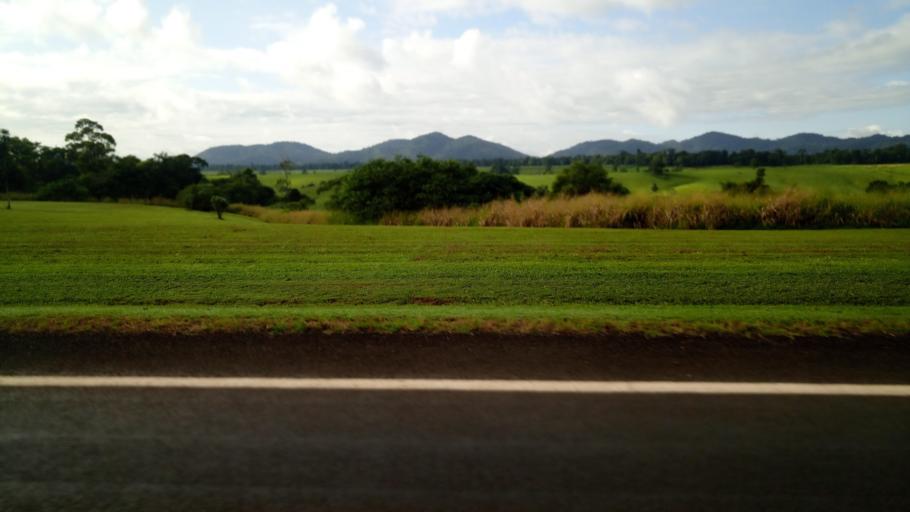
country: AU
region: Queensland
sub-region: Cassowary Coast
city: Innisfail
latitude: -17.6067
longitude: 145.8461
